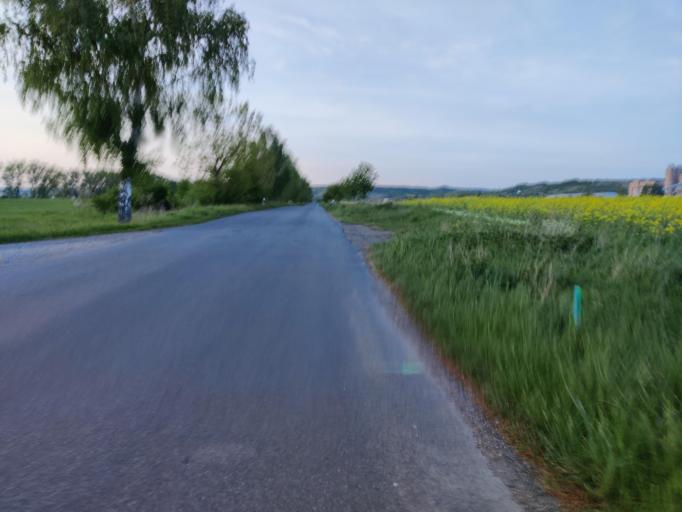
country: DE
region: Saxony-Anhalt
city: Karsdorf
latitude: 51.2656
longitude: 11.6476
